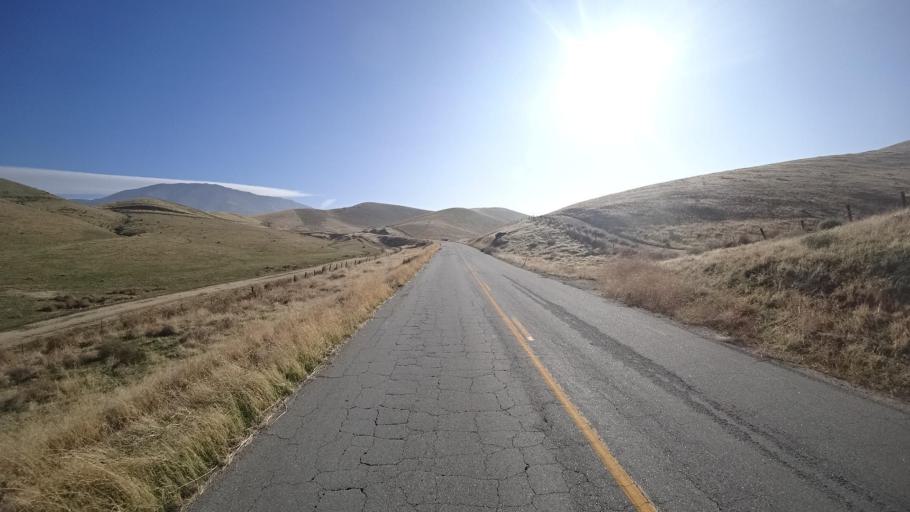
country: US
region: California
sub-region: Kern County
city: Bear Valley Springs
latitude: 35.2829
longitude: -118.6954
